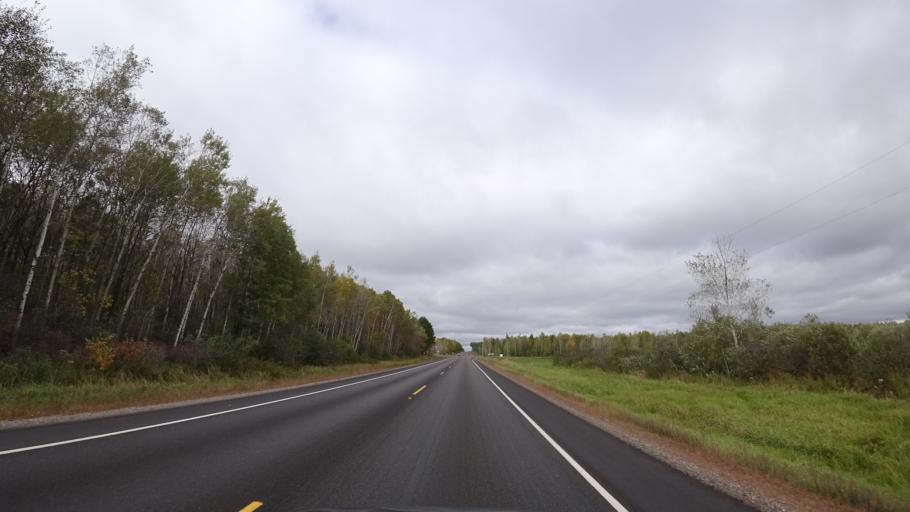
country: US
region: Wisconsin
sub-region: Rusk County
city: Ladysmith
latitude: 45.3336
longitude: -91.1109
